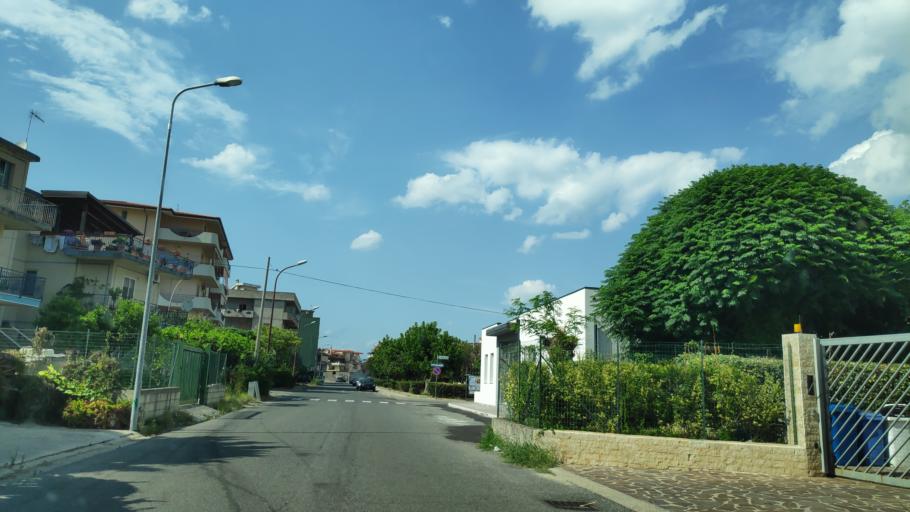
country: IT
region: Calabria
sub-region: Provincia di Catanzaro
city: Marina di Davoli
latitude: 38.6657
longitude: 16.5421
